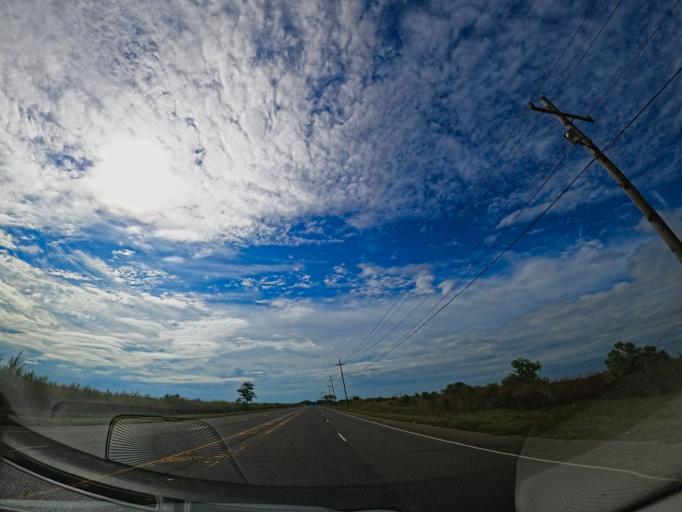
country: US
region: Louisiana
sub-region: Saint Tammany Parish
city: Eden Isle
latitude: 30.0660
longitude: -89.8216
